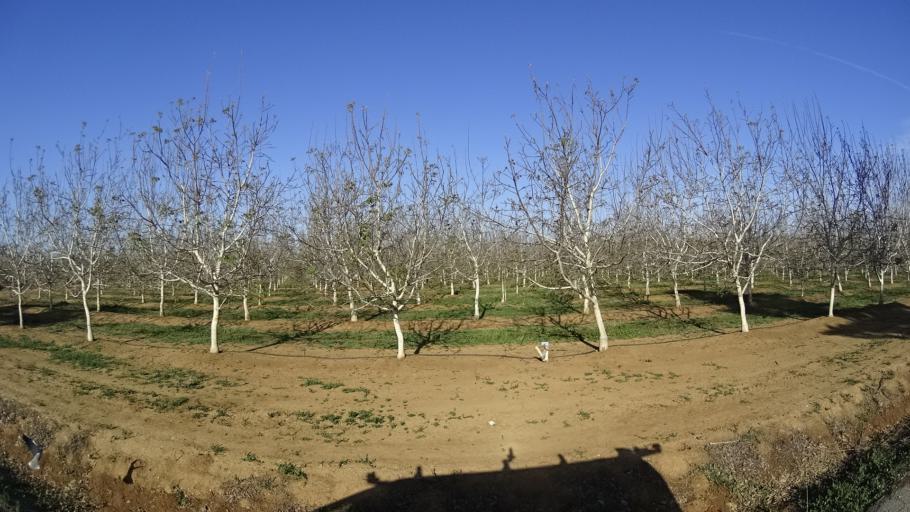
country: US
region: California
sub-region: Glenn County
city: Willows
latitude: 39.5126
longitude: -122.2299
